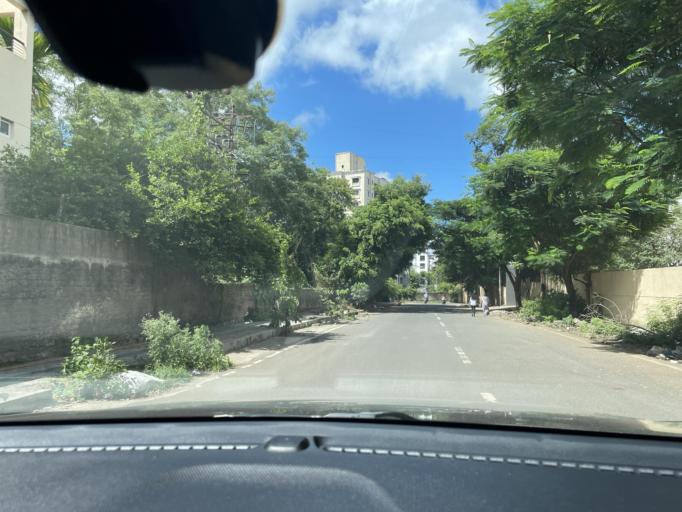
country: IN
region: Maharashtra
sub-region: Pune Division
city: Kharakvasla
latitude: 18.5146
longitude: 73.7774
